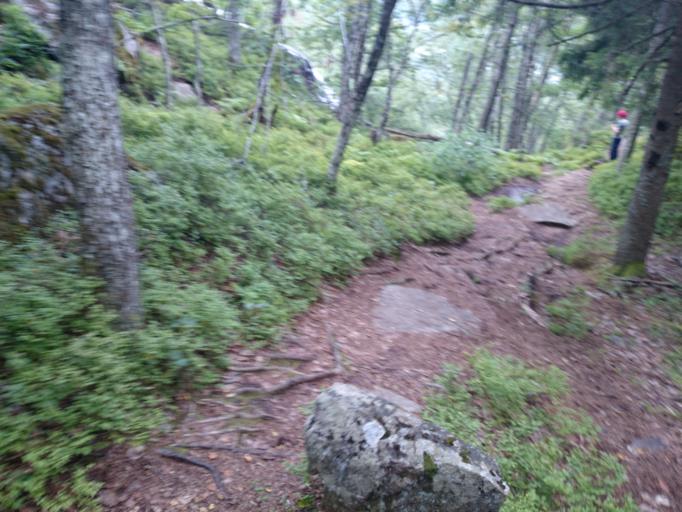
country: NO
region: Aust-Agder
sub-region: Amli
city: Amli
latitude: 58.7691
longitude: 8.4633
